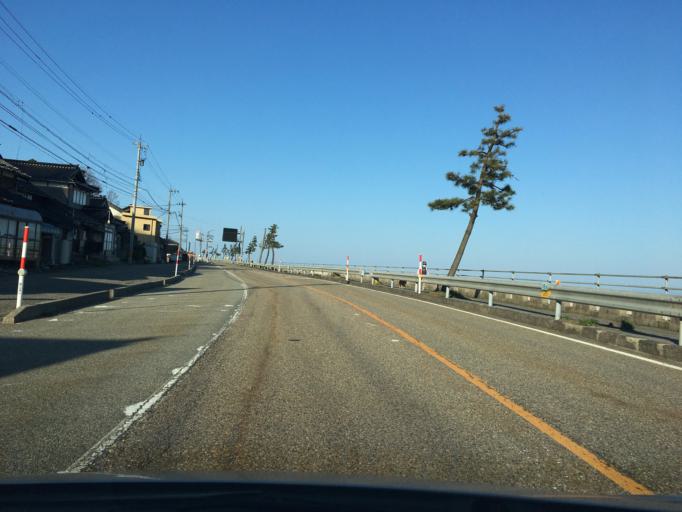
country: JP
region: Ishikawa
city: Nanao
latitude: 36.9629
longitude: 137.0533
